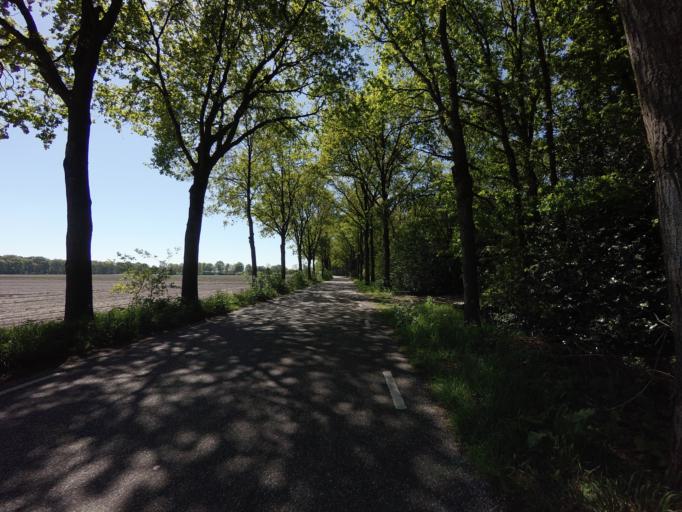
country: BE
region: Flanders
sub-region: Provincie Antwerpen
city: Essen
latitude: 51.4857
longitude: 4.4849
